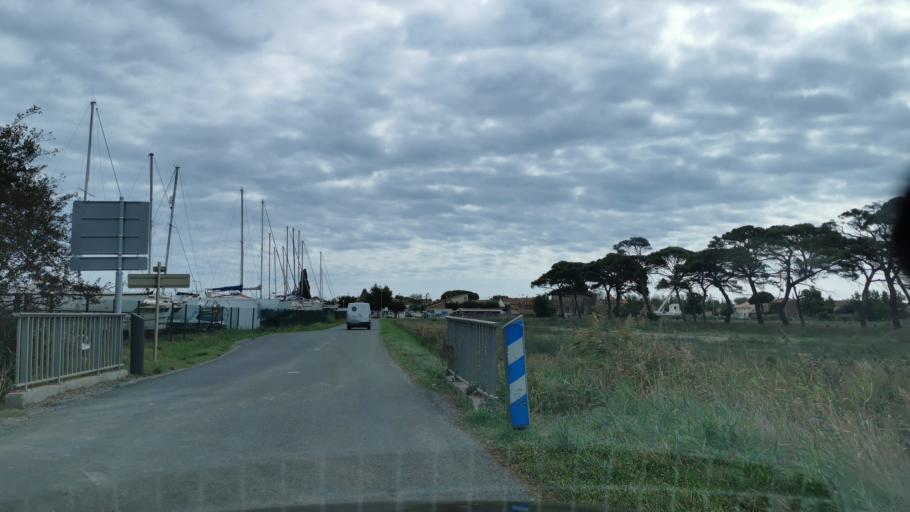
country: FR
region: Languedoc-Roussillon
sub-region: Departement de l'Herault
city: Vendres
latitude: 43.2187
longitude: 3.2272
